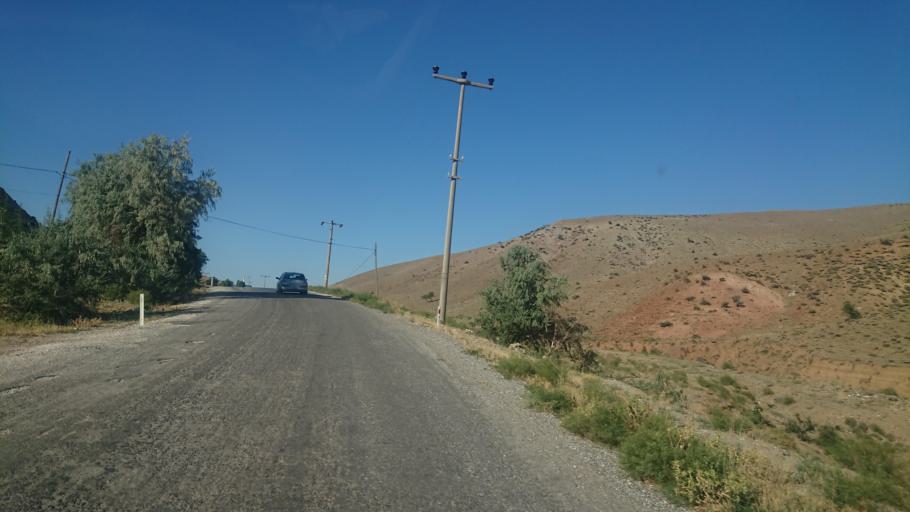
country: TR
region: Ankara
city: Sereflikochisar
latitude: 38.7569
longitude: 33.6947
